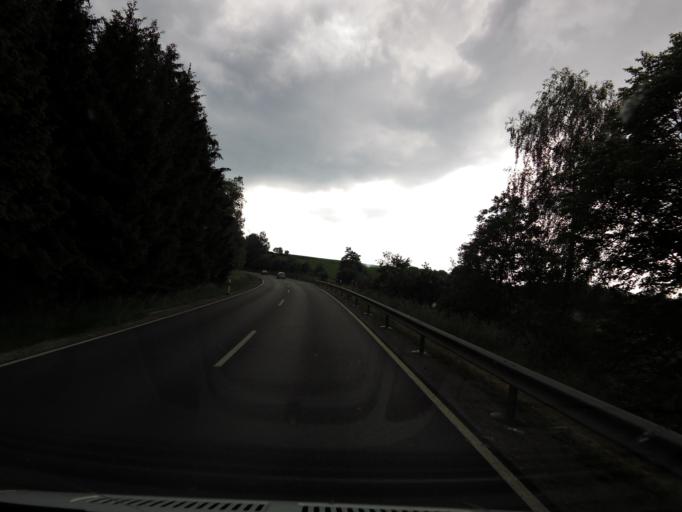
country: DE
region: Bavaria
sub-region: Lower Bavaria
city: Aicha vorm Wald
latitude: 48.6765
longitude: 13.2751
